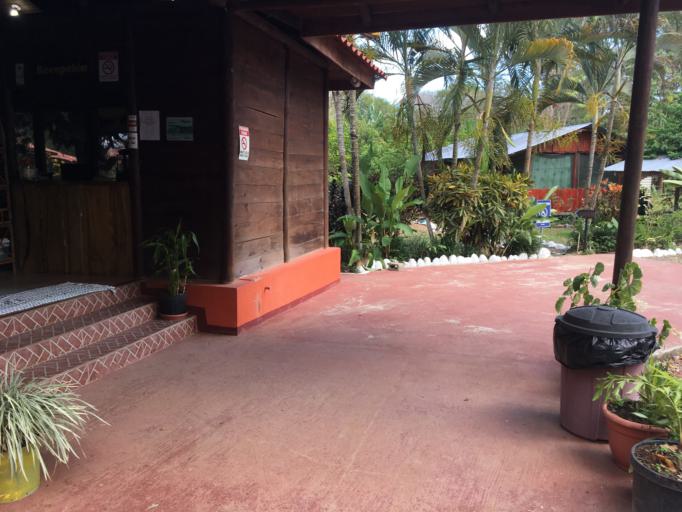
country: CR
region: San Jose
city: Daniel Flores
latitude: 9.1621
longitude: -83.7454
